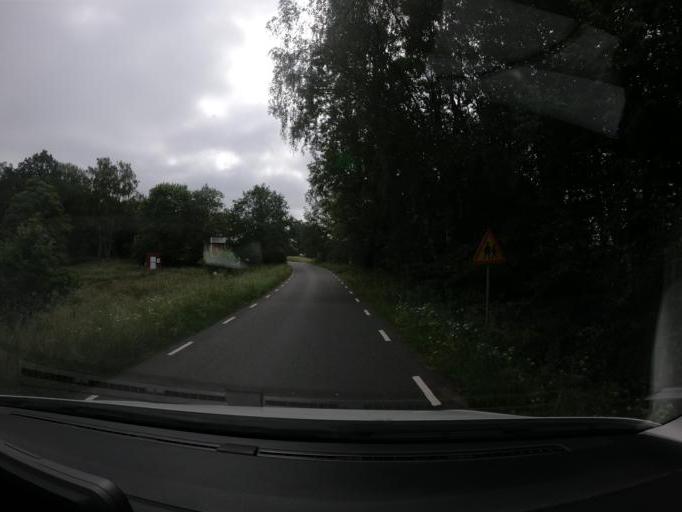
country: SE
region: Skane
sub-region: Eslovs Kommun
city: Stehag
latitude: 55.9822
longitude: 13.4308
